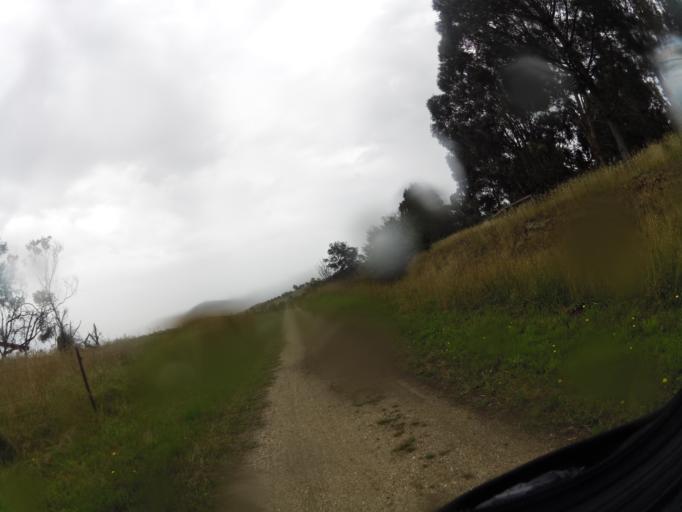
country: AU
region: Victoria
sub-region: East Gippsland
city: Lakes Entrance
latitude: -37.7056
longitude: 147.8230
